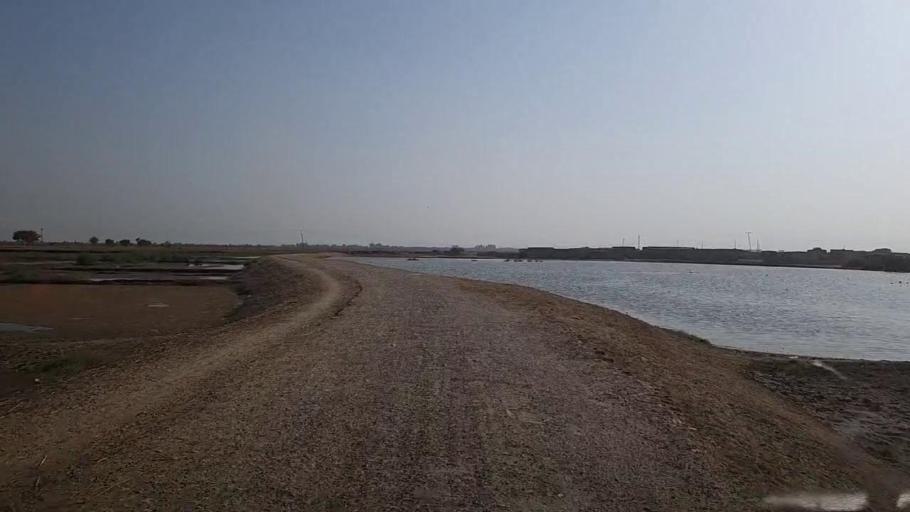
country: PK
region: Sindh
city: Kandhkot
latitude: 28.3716
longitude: 69.3329
